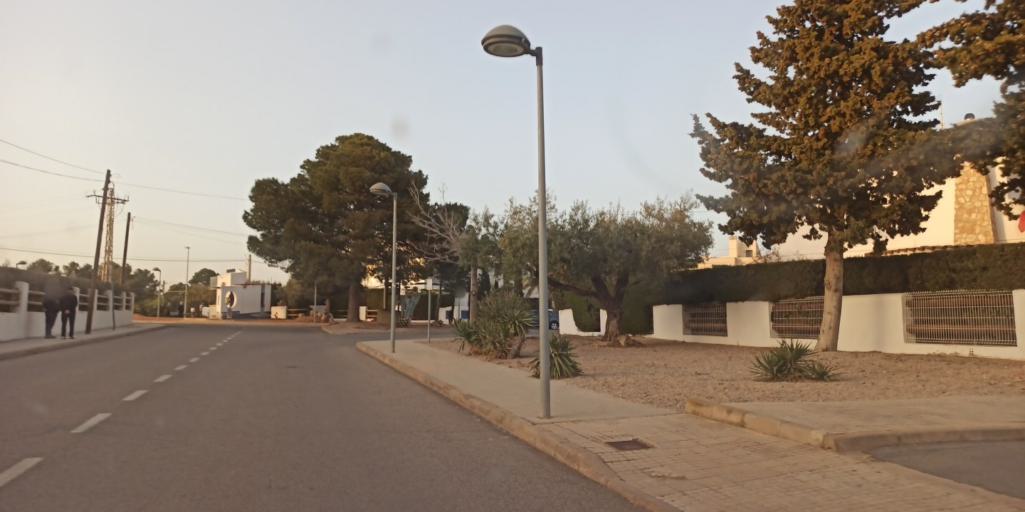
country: ES
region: Catalonia
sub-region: Provincia de Tarragona
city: L'Ampolla
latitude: 40.8237
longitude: 0.7294
